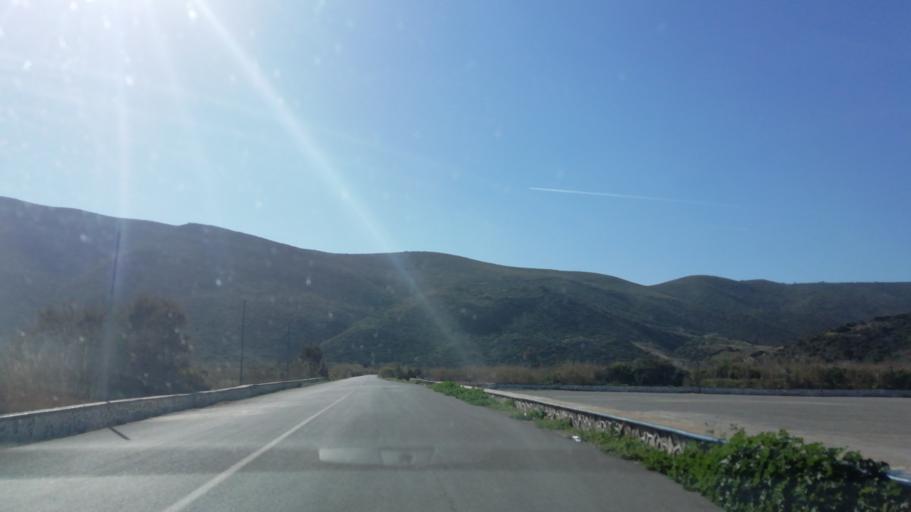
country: DZ
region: Ain Temouchent
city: El Amria
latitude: 35.6384
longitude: -1.0589
